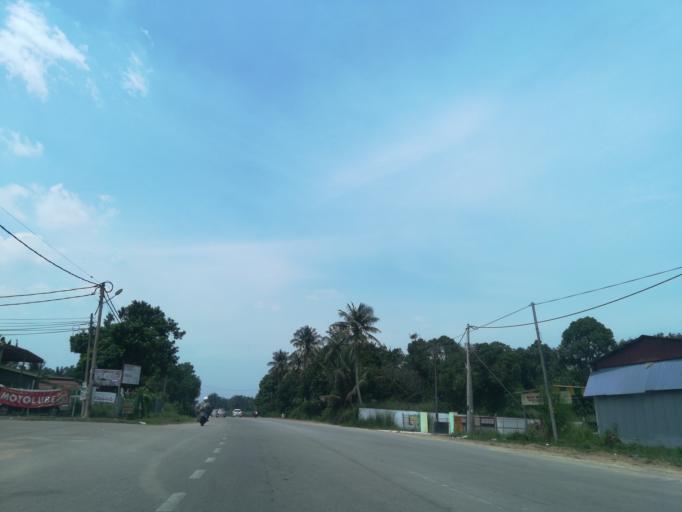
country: MY
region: Penang
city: Tasek Glugor
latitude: 5.4416
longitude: 100.5521
